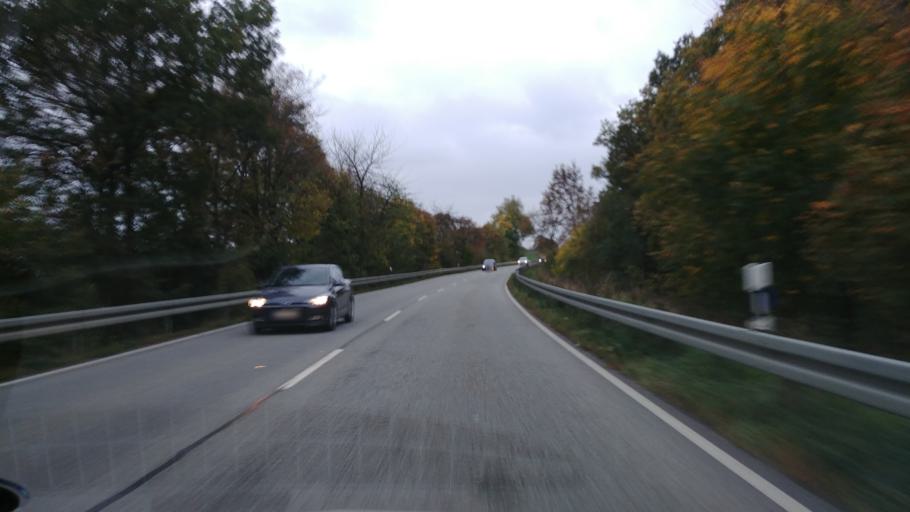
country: DE
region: Hesse
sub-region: Regierungsbezirk Darmstadt
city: Idstein
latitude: 50.2343
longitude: 8.1975
